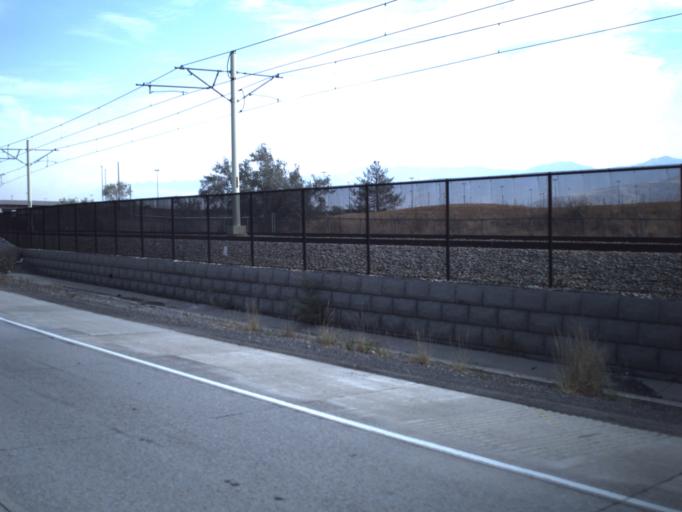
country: US
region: Utah
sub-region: Salt Lake County
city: West Valley City
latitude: 40.7709
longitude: -111.9860
